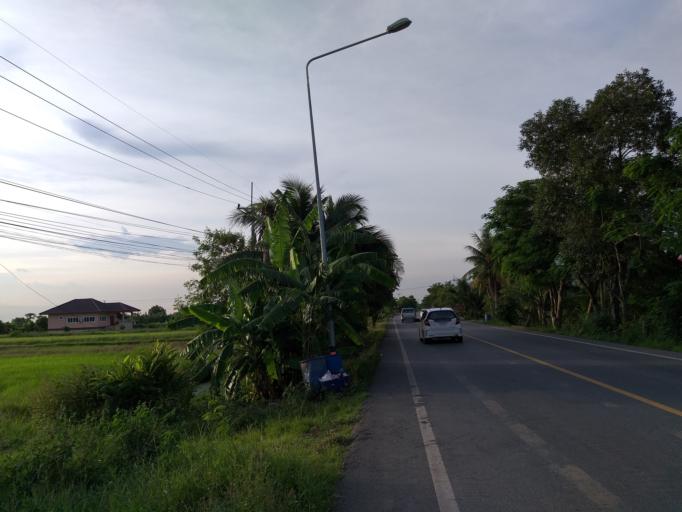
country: TH
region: Pathum Thani
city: Ban Lam Luk Ka
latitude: 14.0084
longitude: 100.8423
